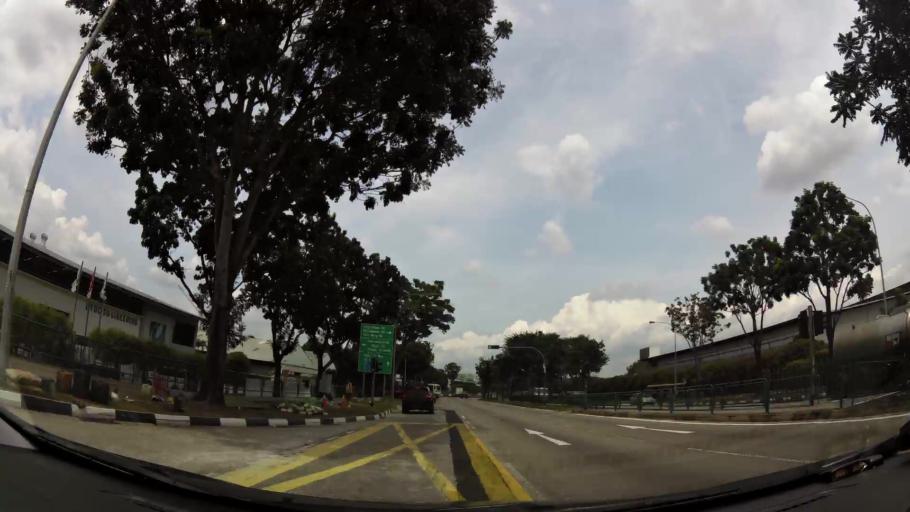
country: SG
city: Singapore
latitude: 1.3264
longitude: 103.7089
